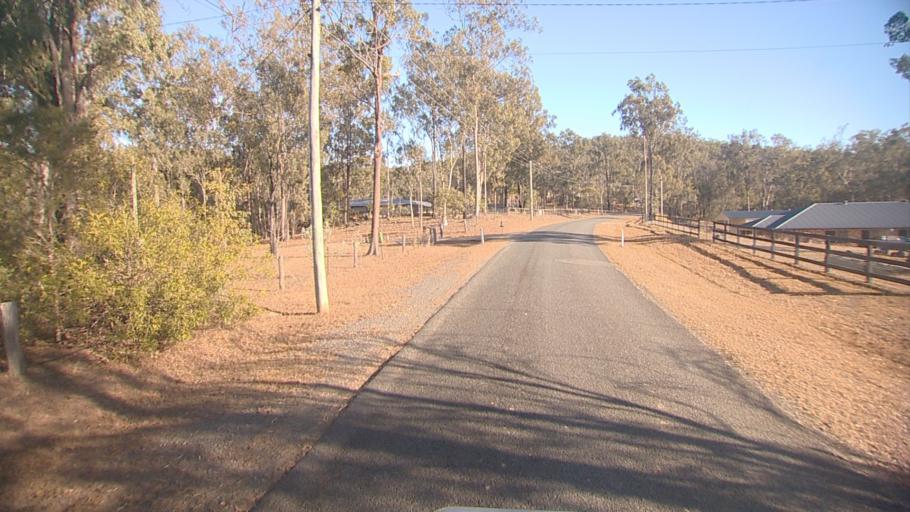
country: AU
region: Queensland
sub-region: Logan
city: Cedar Vale
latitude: -27.8544
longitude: 153.0838
